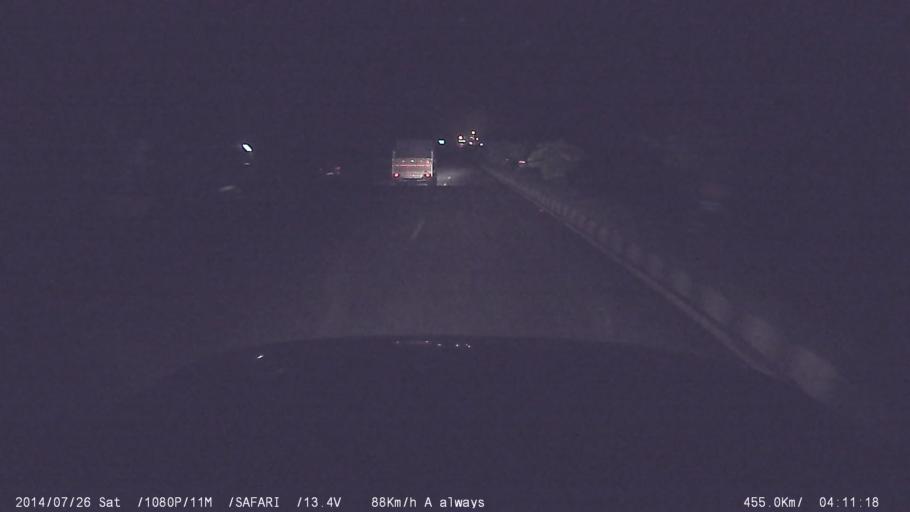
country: IN
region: Kerala
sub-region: Thrissur District
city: Trichur
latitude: 10.5085
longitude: 76.2584
